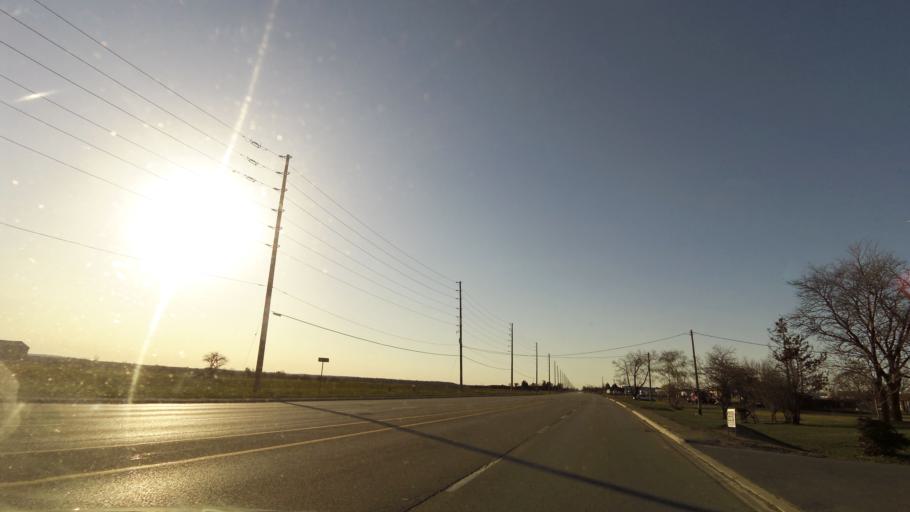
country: CA
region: Ontario
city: Brampton
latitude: 43.8394
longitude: -79.7065
